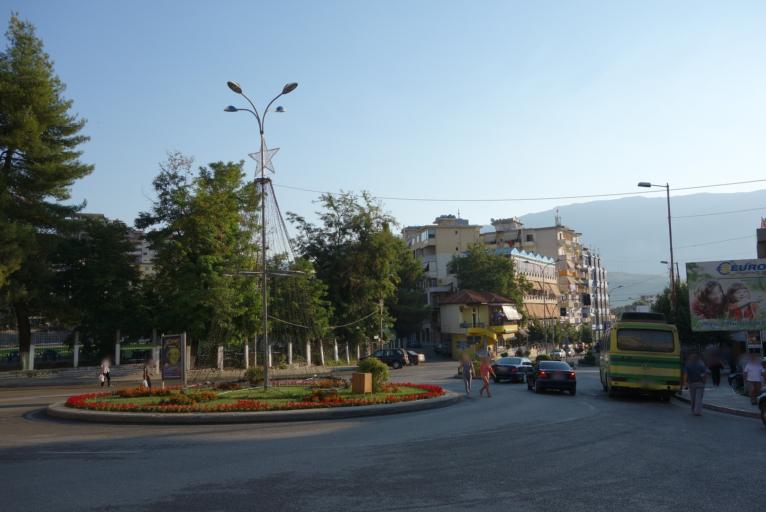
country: AL
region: Gjirokaster
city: Gjirokaster
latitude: 40.0800
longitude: 20.1382
